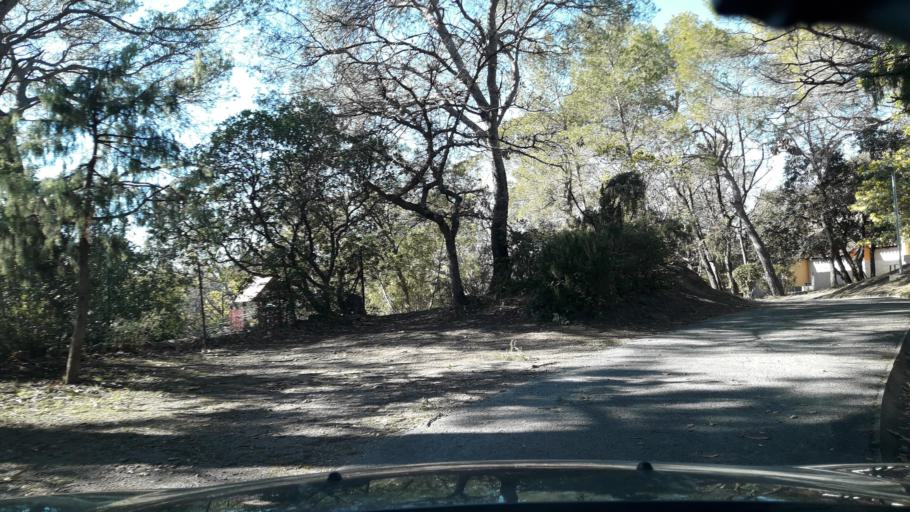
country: FR
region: Provence-Alpes-Cote d'Azur
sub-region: Departement du Var
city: Saint-Raphael
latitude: 43.4439
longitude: 6.7678
